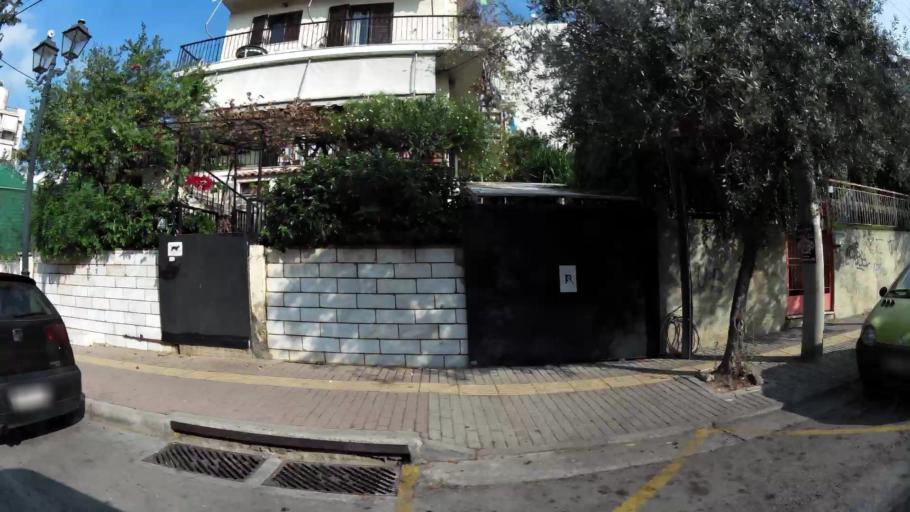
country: GR
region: Attica
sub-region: Nomarchia Athinas
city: Cholargos
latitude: 38.0070
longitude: 23.8124
